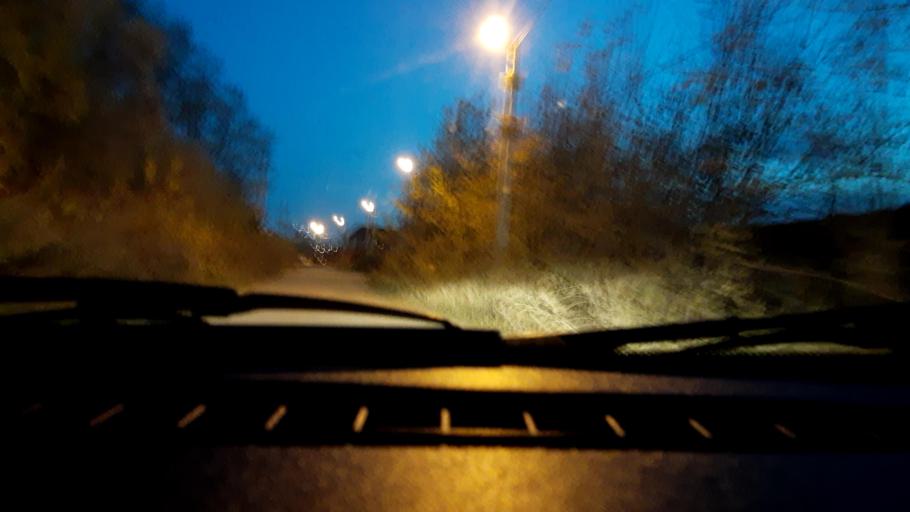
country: RU
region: Bashkortostan
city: Mikhaylovka
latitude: 54.7597
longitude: 55.9134
